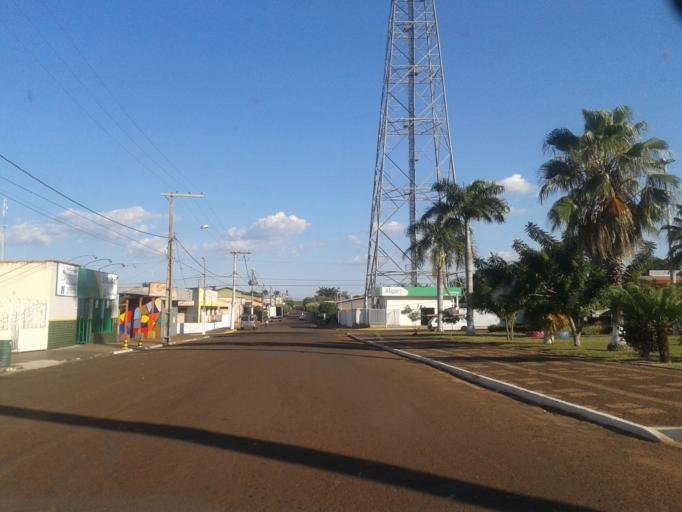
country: BR
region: Minas Gerais
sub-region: Santa Vitoria
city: Santa Vitoria
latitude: -18.6919
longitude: -49.9429
